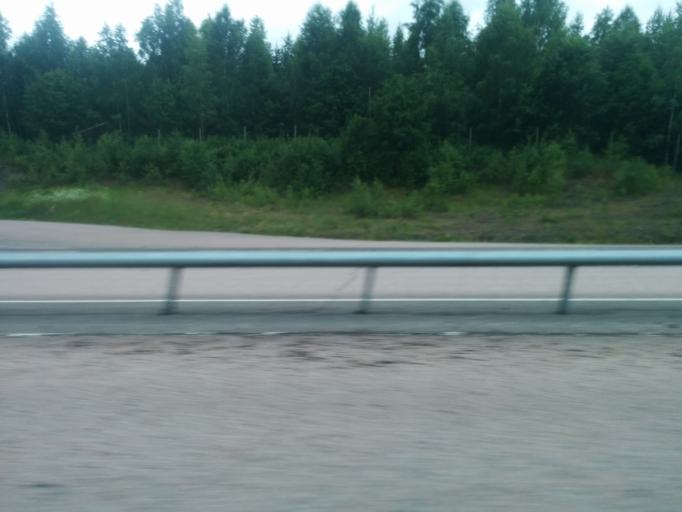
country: FI
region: Pirkanmaa
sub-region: Tampere
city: Orivesi
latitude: 61.7095
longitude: 24.5342
